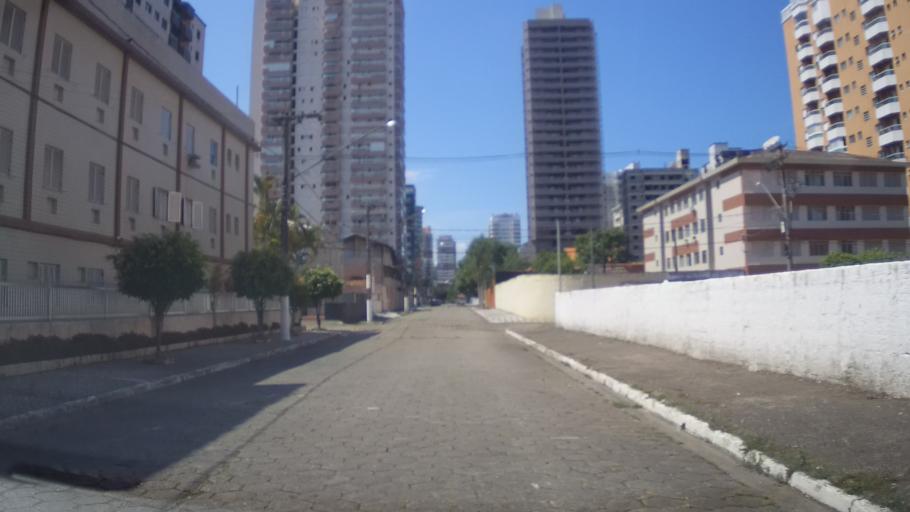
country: BR
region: Sao Paulo
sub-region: Praia Grande
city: Praia Grande
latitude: -24.0136
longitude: -46.4308
